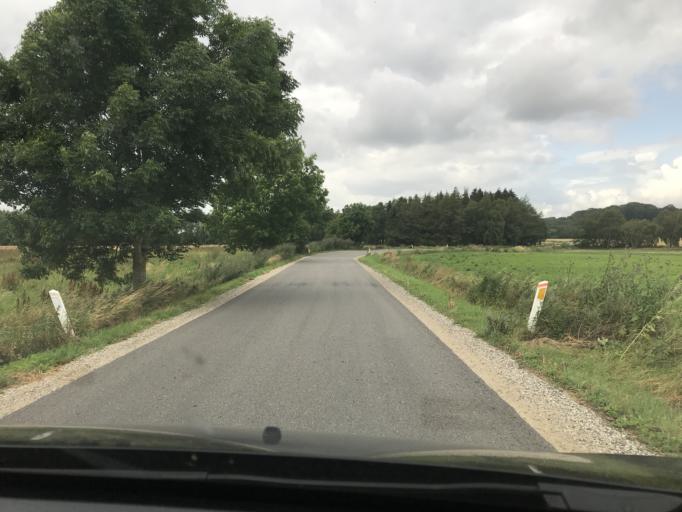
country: DK
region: Central Jutland
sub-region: Syddjurs Kommune
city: Ryomgard
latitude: 56.3806
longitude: 10.4311
